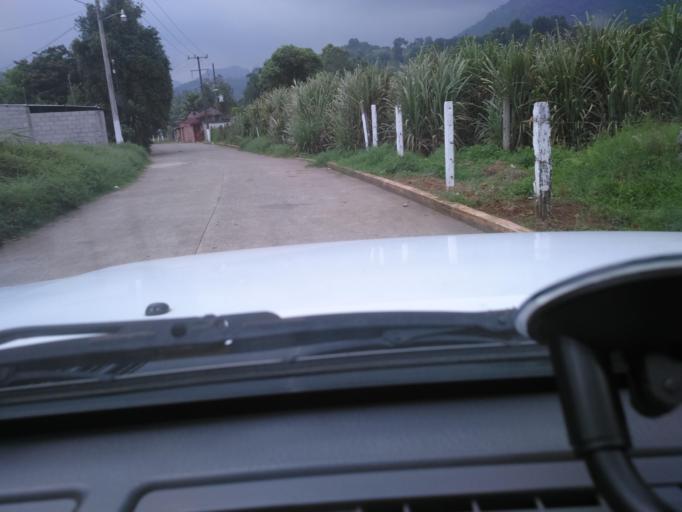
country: MX
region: Veracruz
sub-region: Mariano Escobedo
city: Chicola
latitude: 18.9091
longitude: -97.1075
